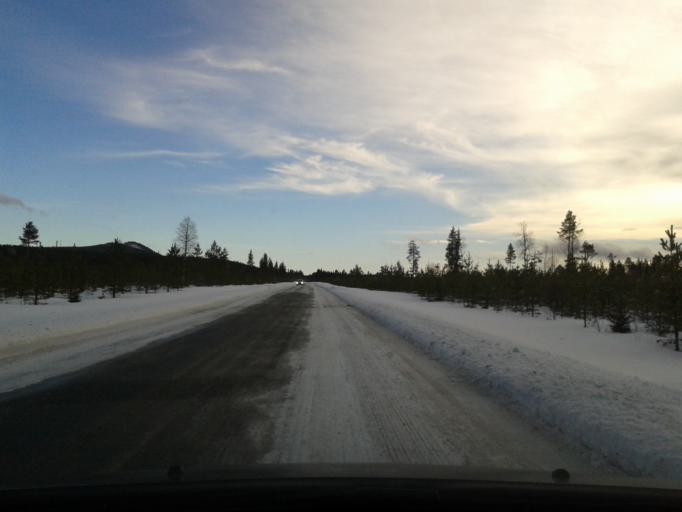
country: SE
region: Vaesterbotten
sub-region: Asele Kommun
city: Asele
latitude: 64.2358
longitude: 17.2954
